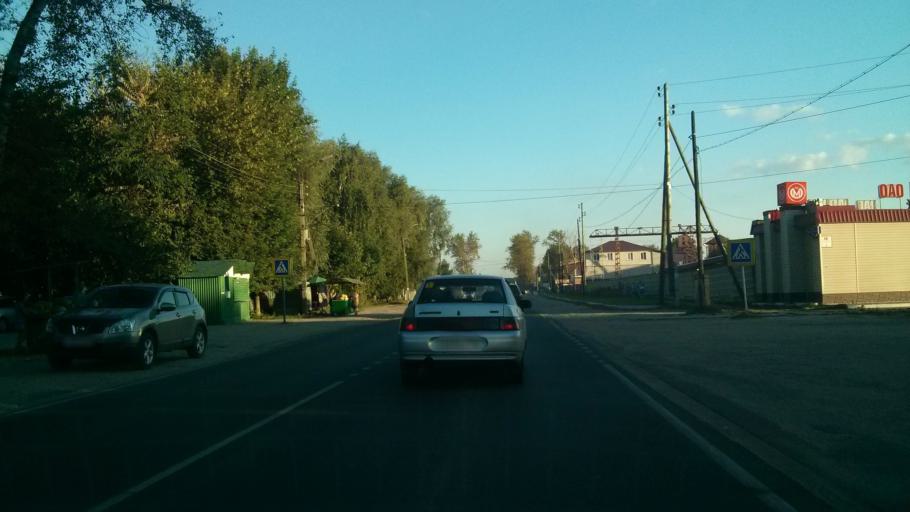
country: RU
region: Vladimir
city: Murom
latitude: 55.5956
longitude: 42.0340
